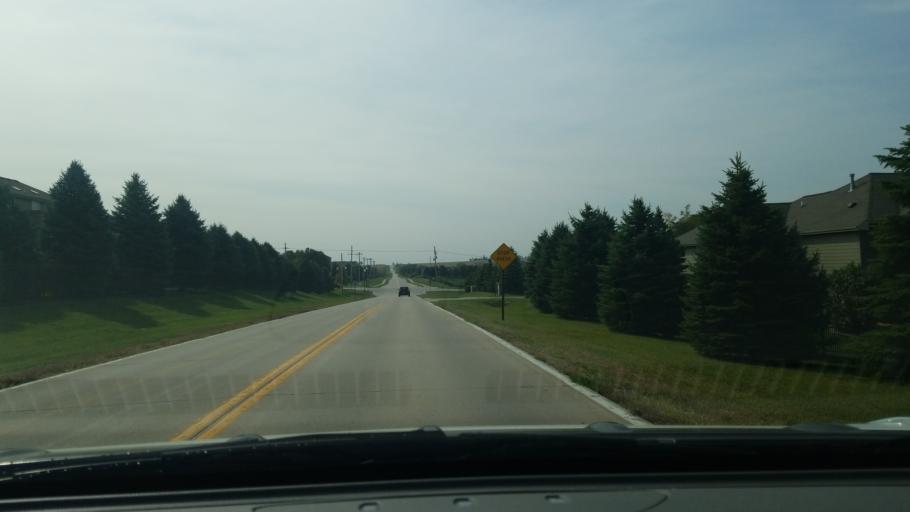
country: US
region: Nebraska
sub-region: Sarpy County
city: Papillion
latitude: 41.1346
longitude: -96.0621
